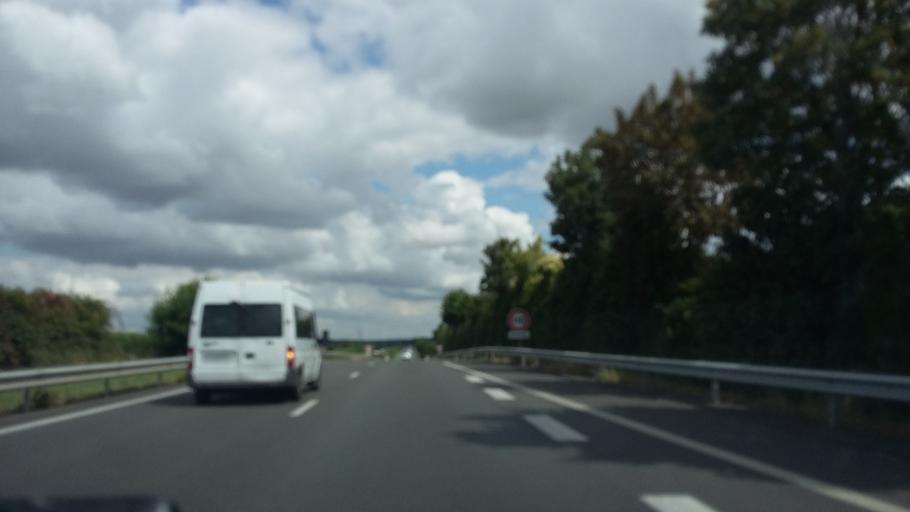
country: FR
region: Poitou-Charentes
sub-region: Departement de la Vienne
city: Couhe
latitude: 46.3310
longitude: 0.1864
